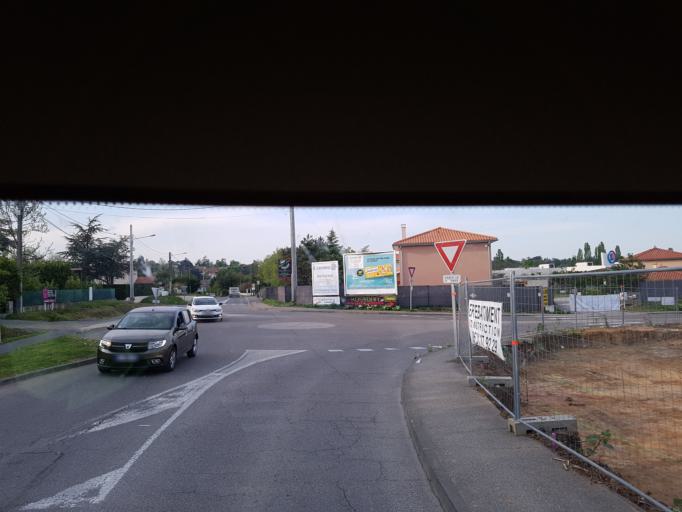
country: FR
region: Rhone-Alpes
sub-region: Departement du Rhone
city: Grezieu-la-Varenne
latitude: 45.7408
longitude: 4.6908
